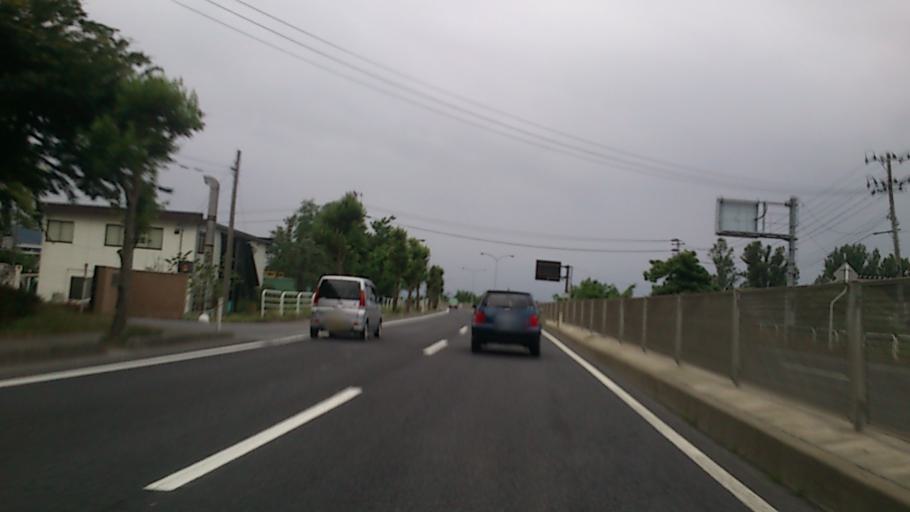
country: JP
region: Yamagata
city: Tendo
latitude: 38.3215
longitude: 140.3629
